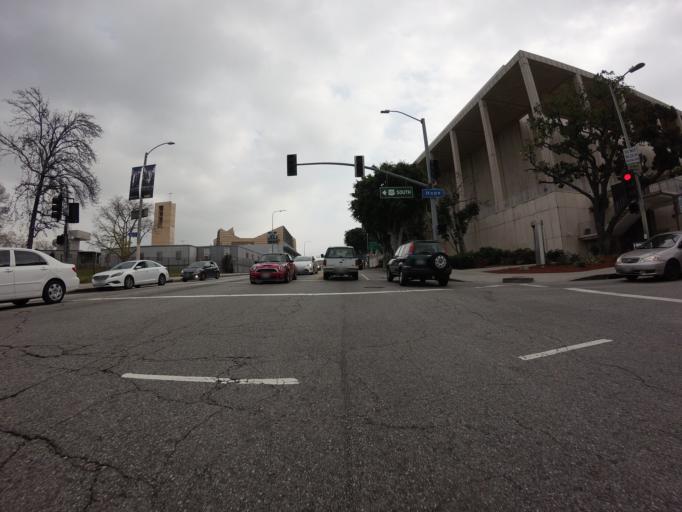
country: US
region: California
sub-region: Los Angeles County
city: Los Angeles
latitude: 34.0589
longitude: -118.2474
